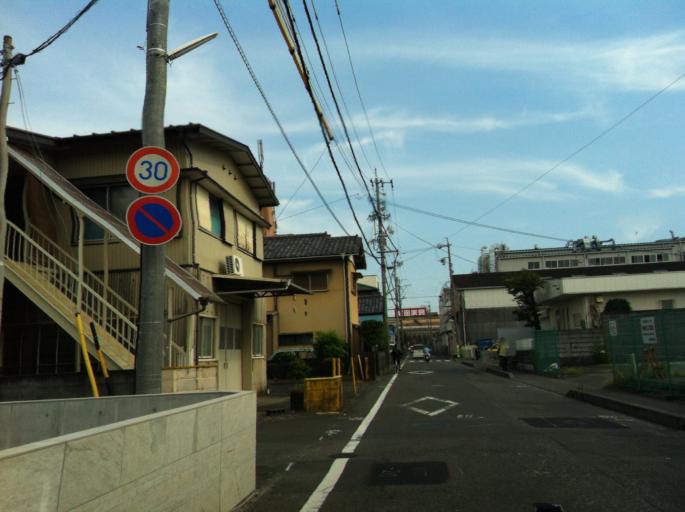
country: JP
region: Shizuoka
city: Shizuoka-shi
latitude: 35.0191
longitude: 138.4612
